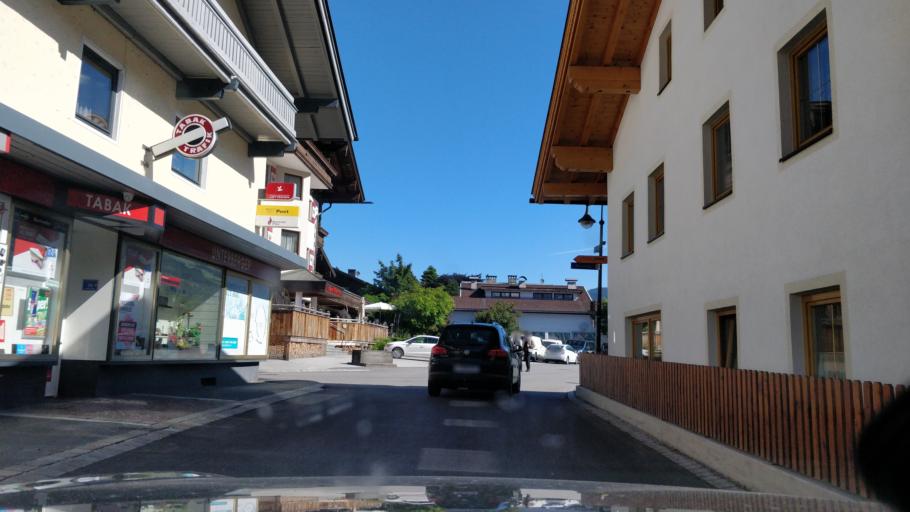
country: AT
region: Tyrol
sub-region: Politischer Bezirk Schwaz
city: Uderns
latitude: 47.3246
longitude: 11.8644
